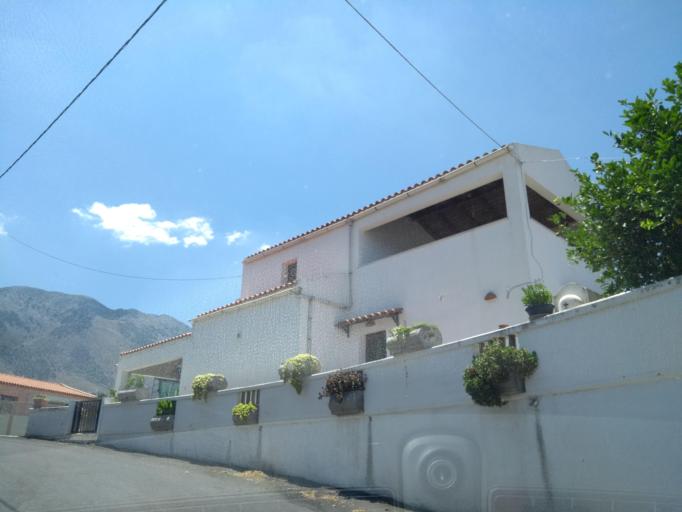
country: GR
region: Crete
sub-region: Nomos Chanias
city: Georgioupolis
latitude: 35.3173
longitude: 24.3092
